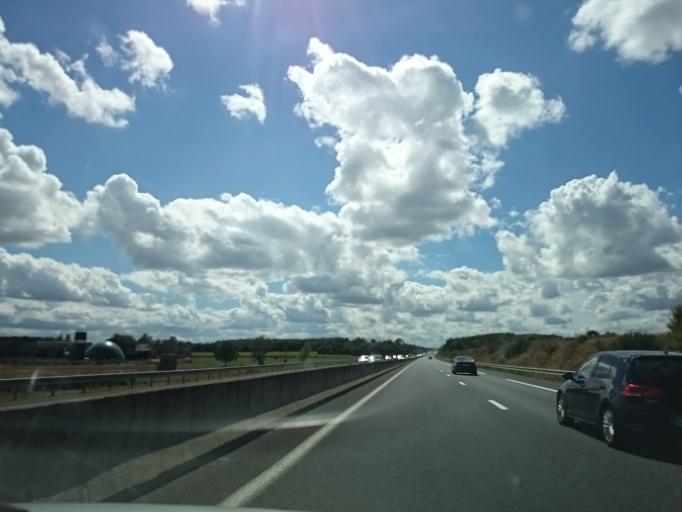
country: FR
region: Pays de la Loire
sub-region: Departement de Maine-et-Loire
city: Saint-Lambert-la-Potherie
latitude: 47.4791
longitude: -0.6697
